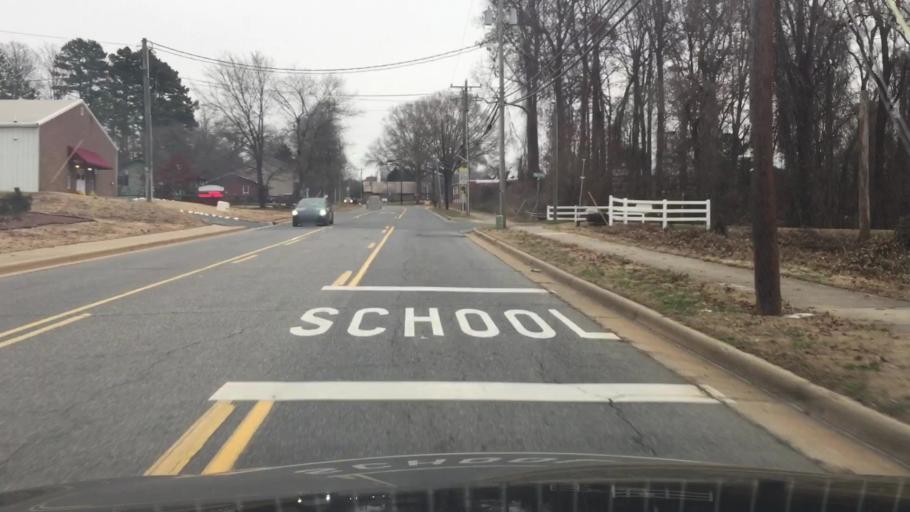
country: US
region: North Carolina
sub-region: Iredell County
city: Mooresville
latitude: 35.5876
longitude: -80.8260
